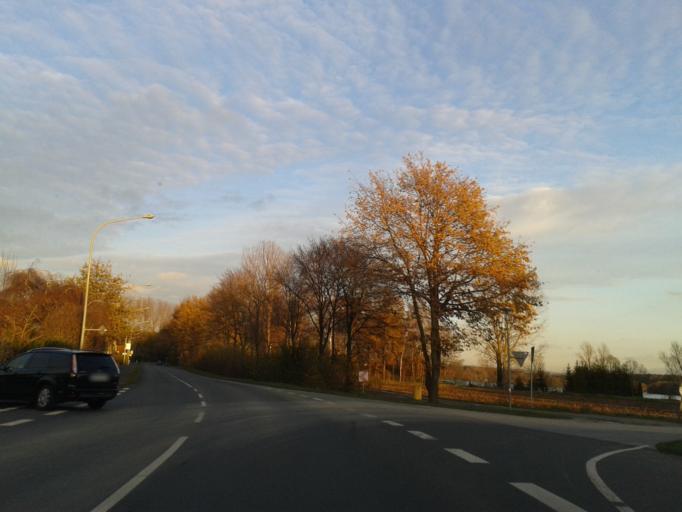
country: DE
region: North Rhine-Westphalia
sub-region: Regierungsbezirk Detmold
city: Hovelhof
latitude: 51.7587
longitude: 8.6704
